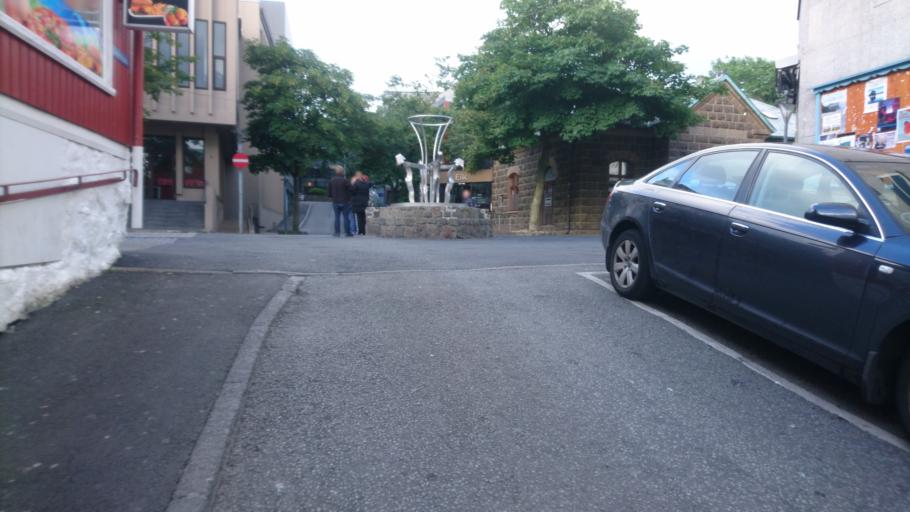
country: FO
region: Streymoy
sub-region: Torshavn
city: Torshavn
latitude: 62.0109
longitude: -6.7733
